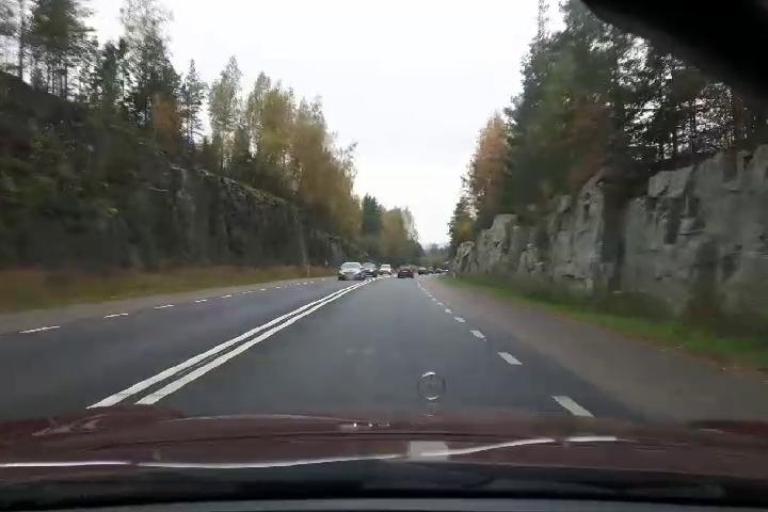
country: SE
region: Vaesternorrland
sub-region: OErnskoeldsviks Kommun
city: Ornskoldsvik
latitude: 63.2957
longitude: 18.6696
